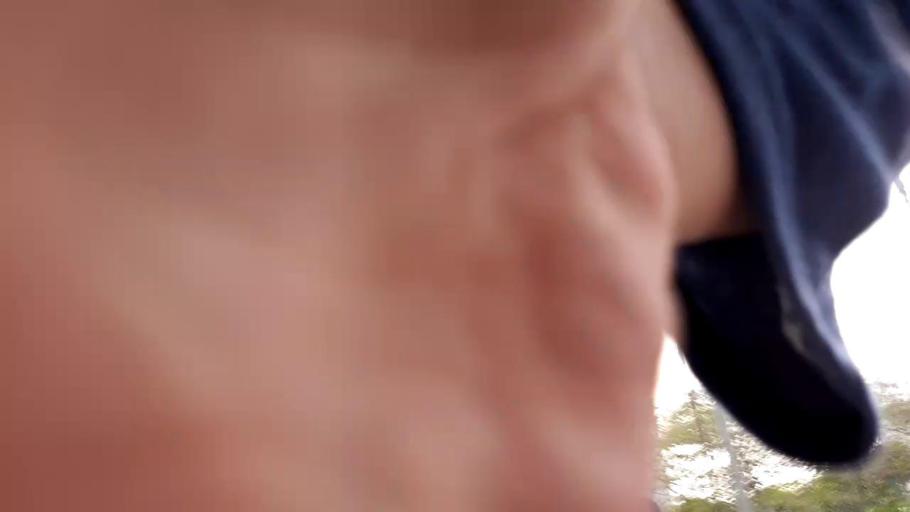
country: VN
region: Ha Noi
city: Cau Giay
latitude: 21.0414
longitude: 105.7978
